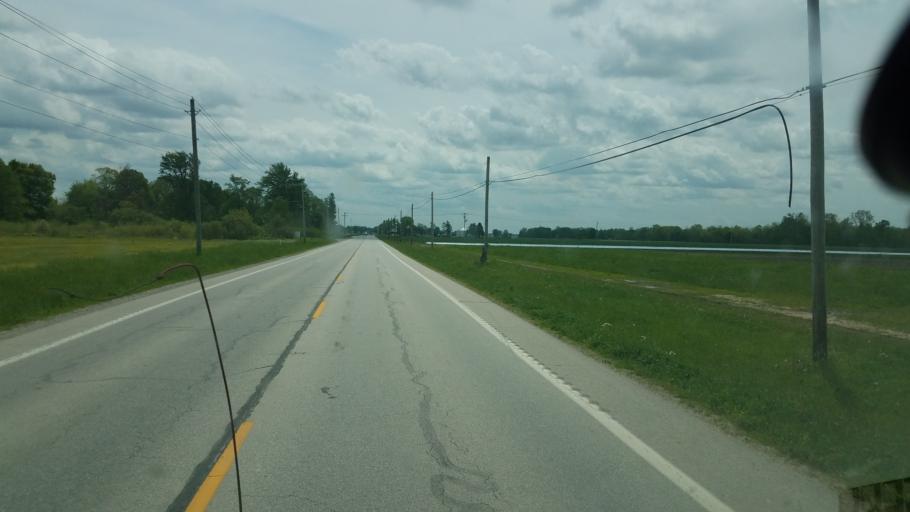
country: US
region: Ohio
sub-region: Sandusky County
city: Ballville
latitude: 41.2288
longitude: -83.1678
